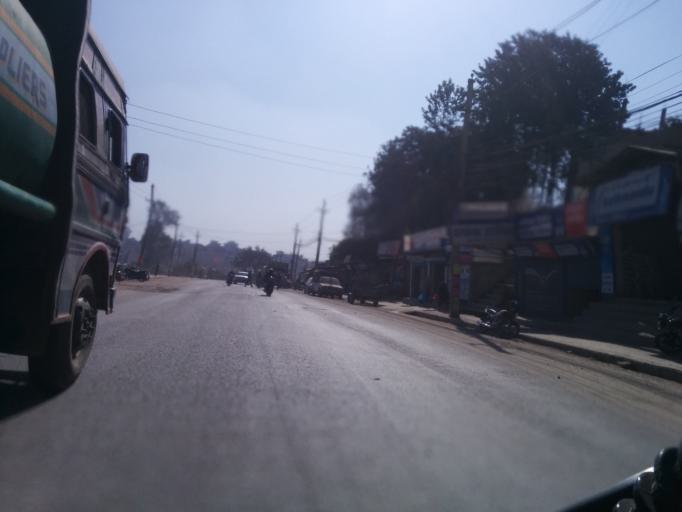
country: NP
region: Central Region
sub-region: Bagmati Zone
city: Patan
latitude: 27.6835
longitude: 85.2979
